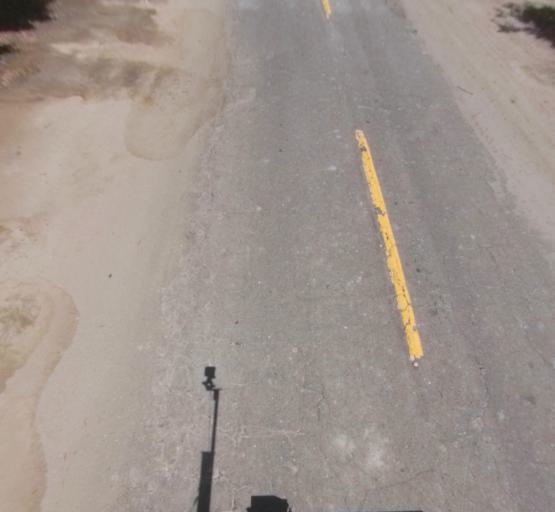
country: US
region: California
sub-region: Madera County
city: Chowchilla
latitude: 37.0690
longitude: -120.3006
